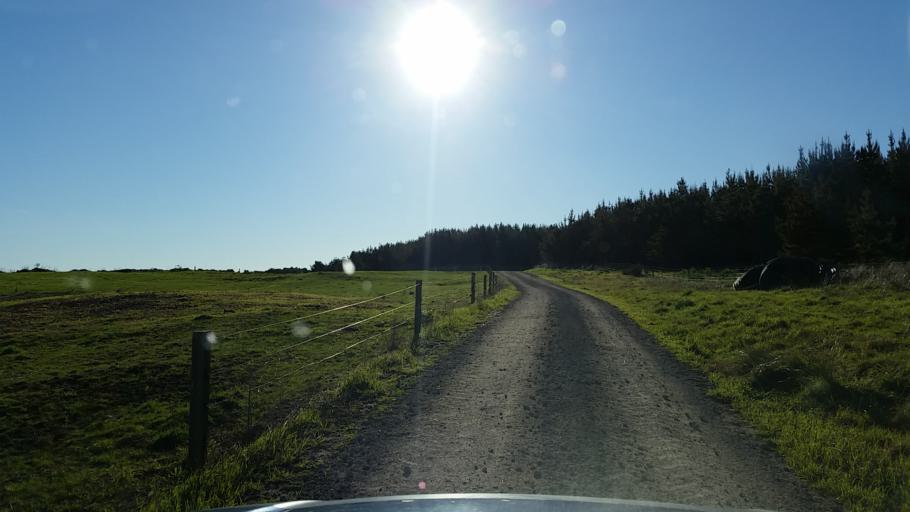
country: NZ
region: Taranaki
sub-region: South Taranaki District
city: Patea
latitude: -39.8345
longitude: 174.6831
